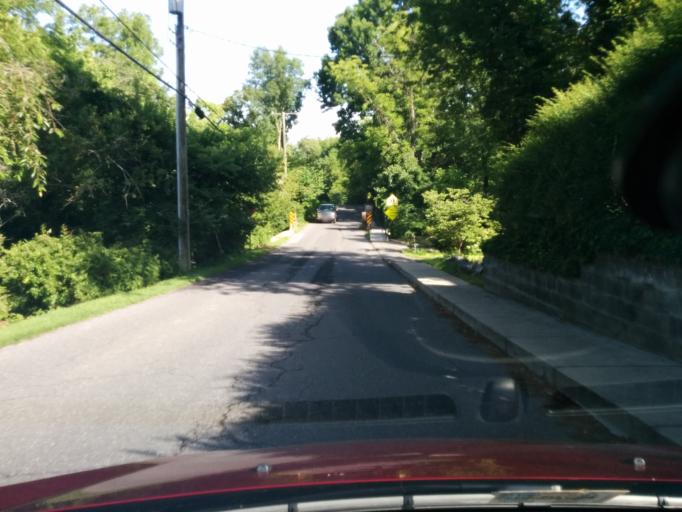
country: US
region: Virginia
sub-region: City of Lexington
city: Lexington
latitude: 37.7797
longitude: -79.4524
